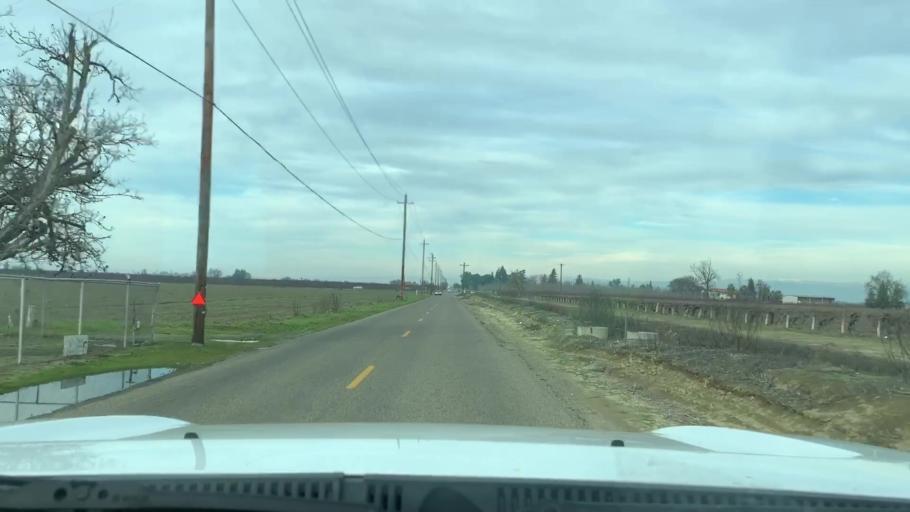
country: US
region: California
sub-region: Fresno County
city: Selma
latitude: 36.5724
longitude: -119.5750
